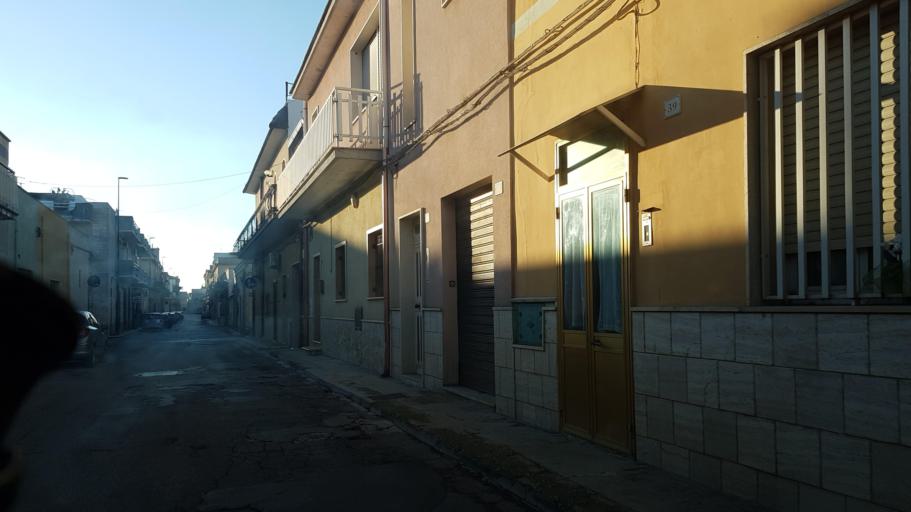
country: IT
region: Apulia
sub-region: Provincia di Brindisi
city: Latiano
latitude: 40.5518
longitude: 17.7232
